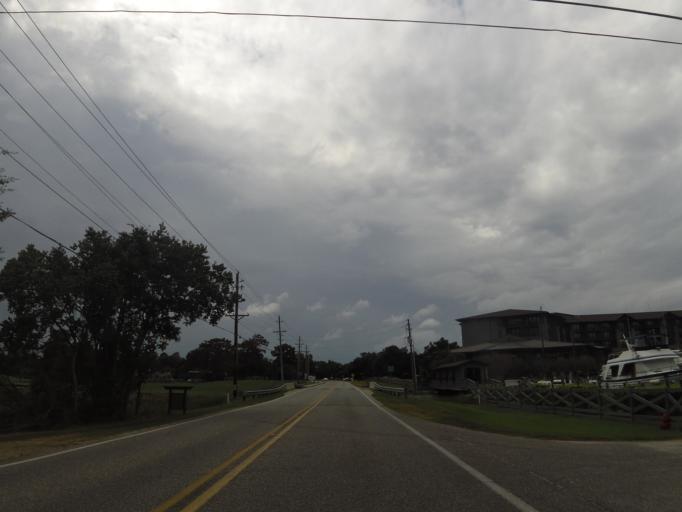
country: US
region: Alabama
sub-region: Baldwin County
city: Point Clear
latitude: 30.4863
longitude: -87.9322
